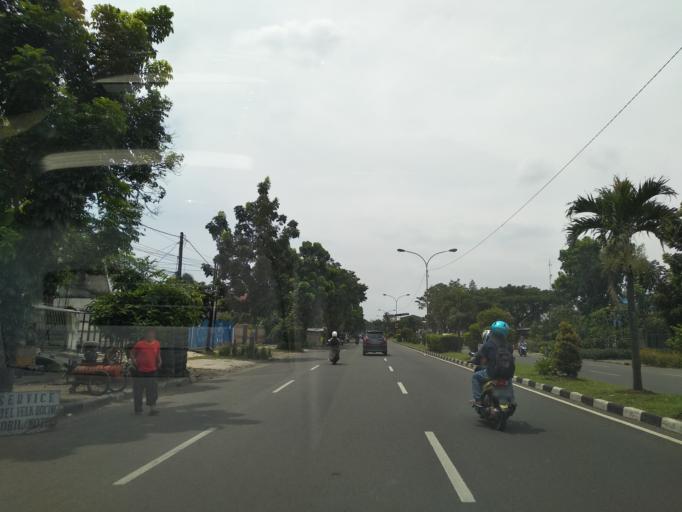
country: ID
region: West Java
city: Bandung
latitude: -6.9380
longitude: 107.6169
